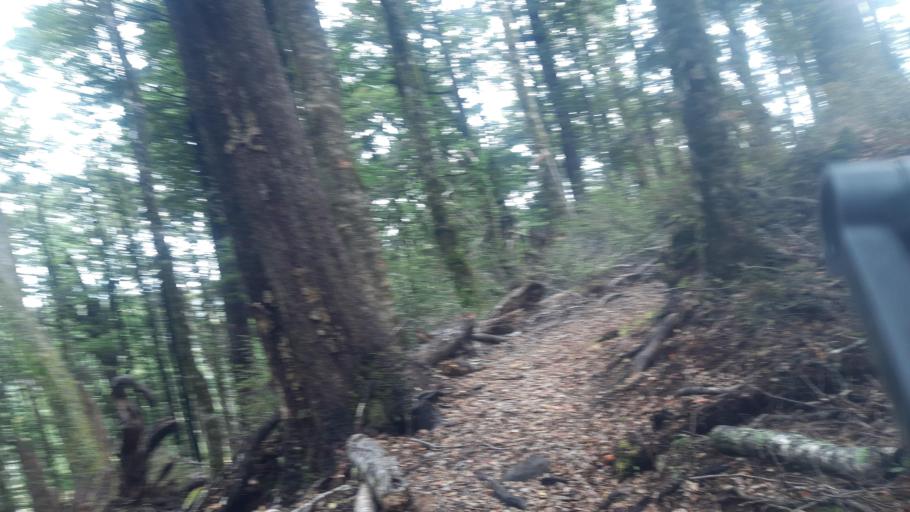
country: NZ
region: Tasman
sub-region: Tasman District
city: Wakefield
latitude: -41.7690
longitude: 172.8178
